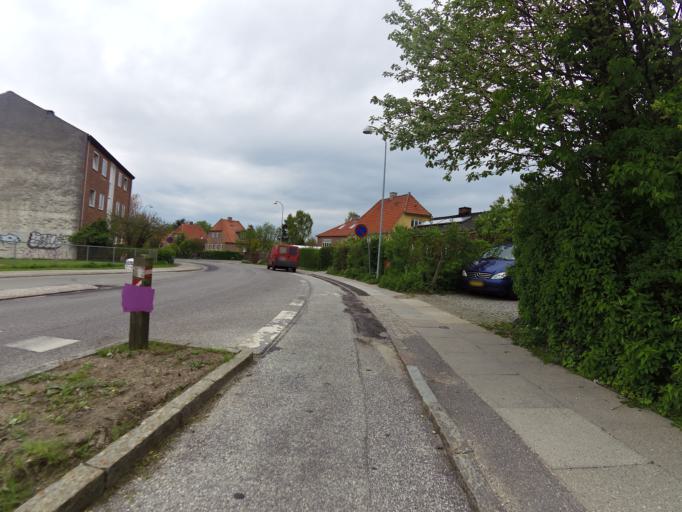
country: DK
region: Capital Region
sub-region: Gladsaxe Municipality
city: Buddinge
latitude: 55.7439
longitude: 12.4995
